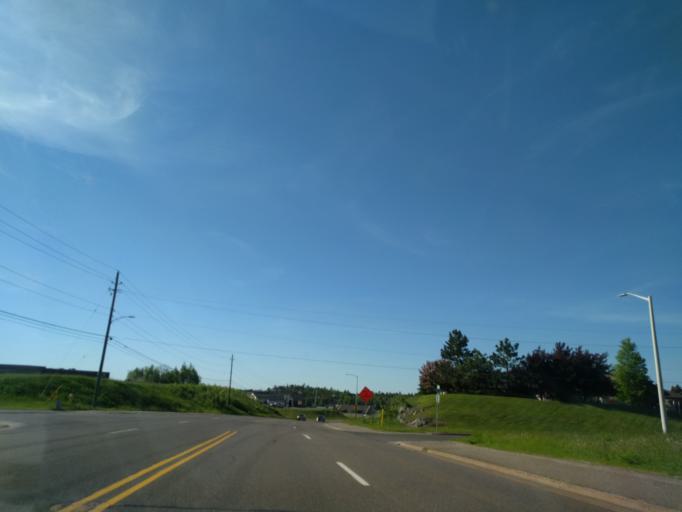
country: US
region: Michigan
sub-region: Marquette County
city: Marquette
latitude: 46.5408
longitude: -87.4190
